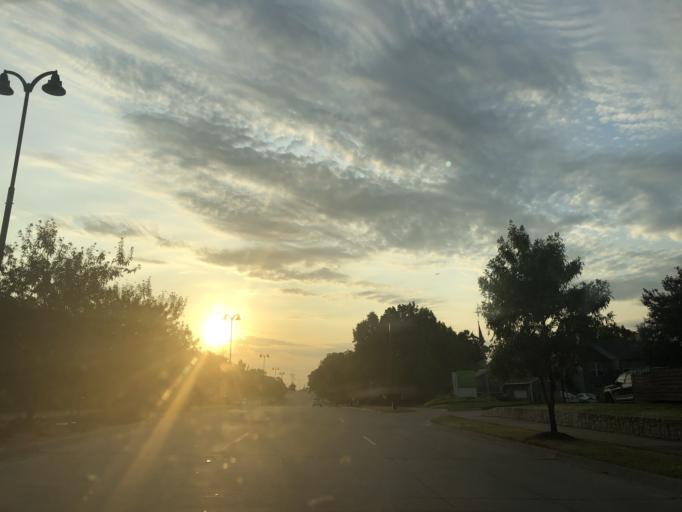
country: US
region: Texas
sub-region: Tarrant County
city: Arlington
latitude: 32.7645
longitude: -97.0932
